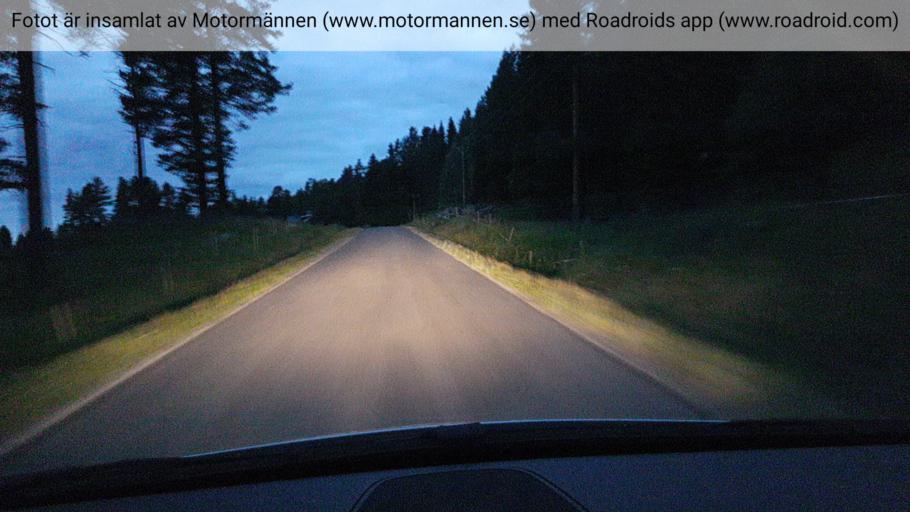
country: SE
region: Jaemtland
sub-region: Braecke Kommun
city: Braecke
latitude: 63.1945
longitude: 15.5059
